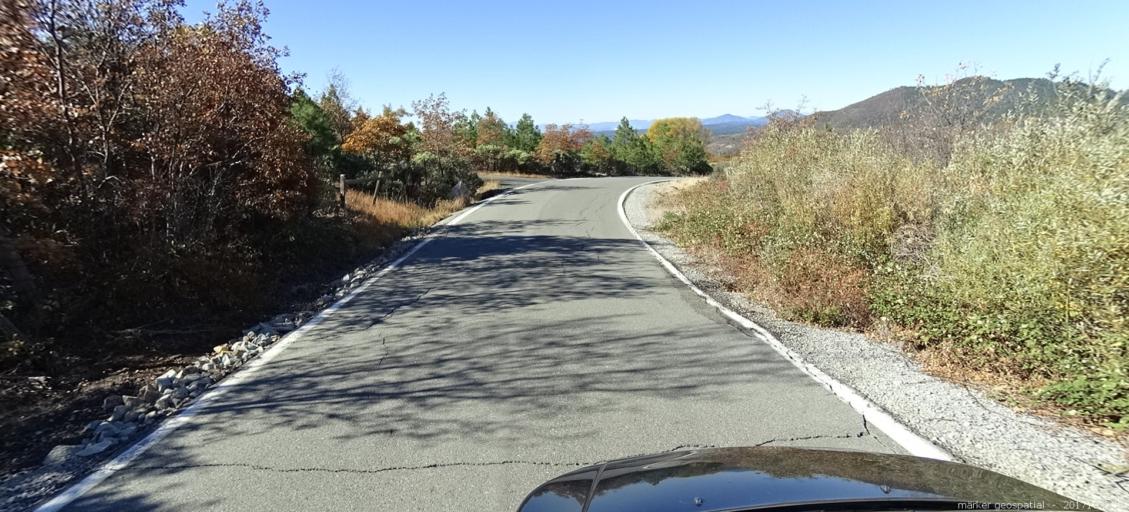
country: US
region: California
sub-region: Shasta County
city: Burney
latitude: 40.7906
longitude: -121.9144
